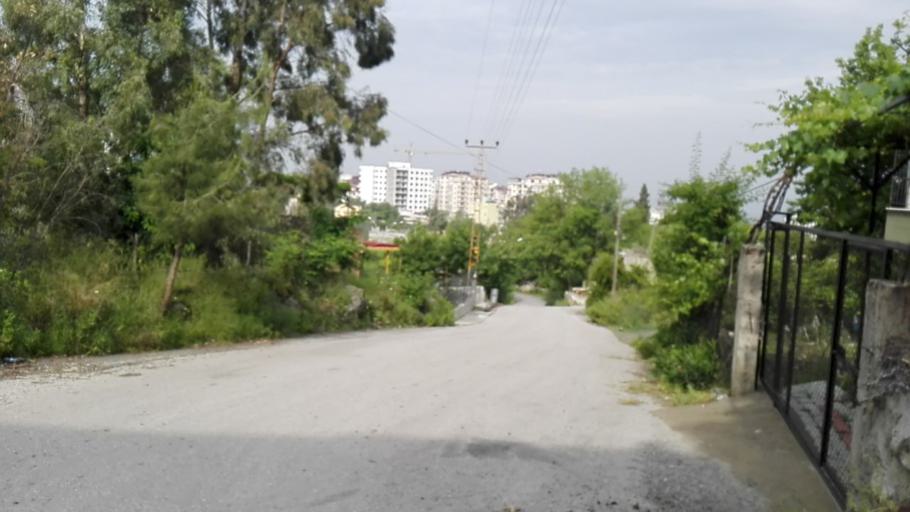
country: TR
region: Osmaniye
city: Haruniye
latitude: 37.2493
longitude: 36.4676
